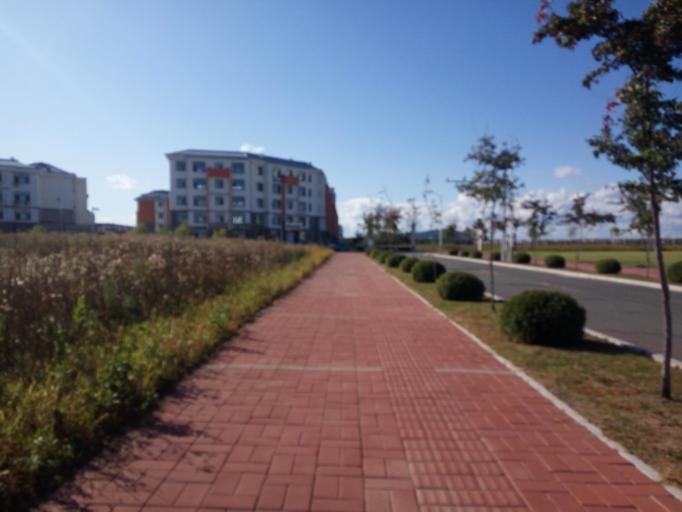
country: CN
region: Heilongjiang Sheng
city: Erjing
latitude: 48.6280
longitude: 126.1151
